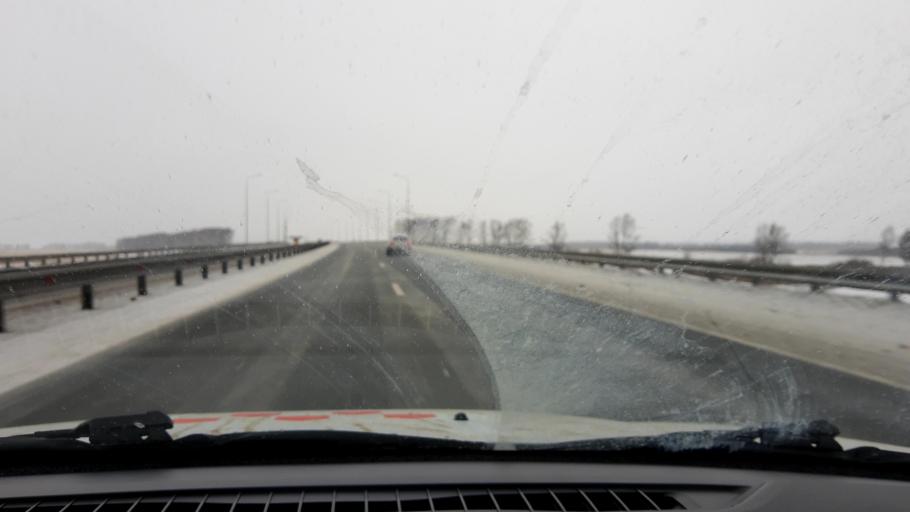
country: RU
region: Nizjnij Novgorod
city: Burevestnik
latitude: 56.1191
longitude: 43.9368
